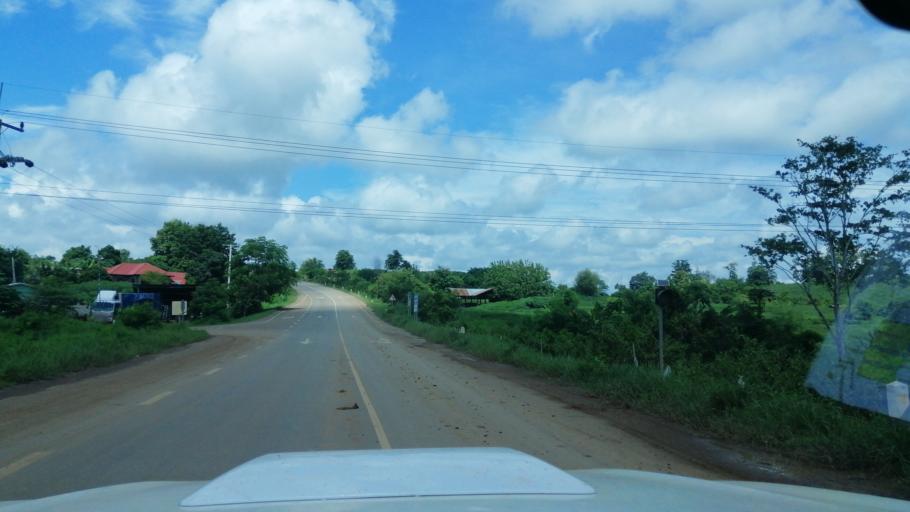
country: TH
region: Uttaradit
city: Ban Khok
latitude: 18.1377
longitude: 101.2832
